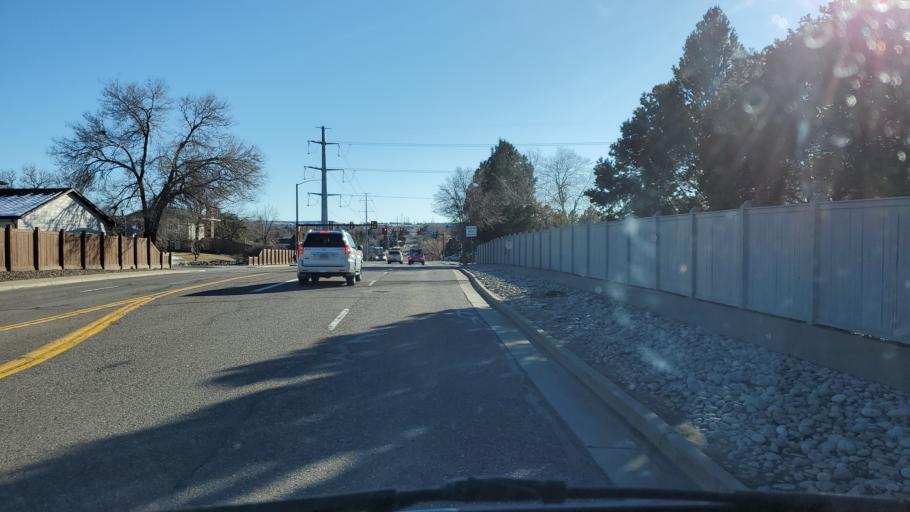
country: US
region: Colorado
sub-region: Arapahoe County
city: Castlewood
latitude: 39.5817
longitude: -104.9043
